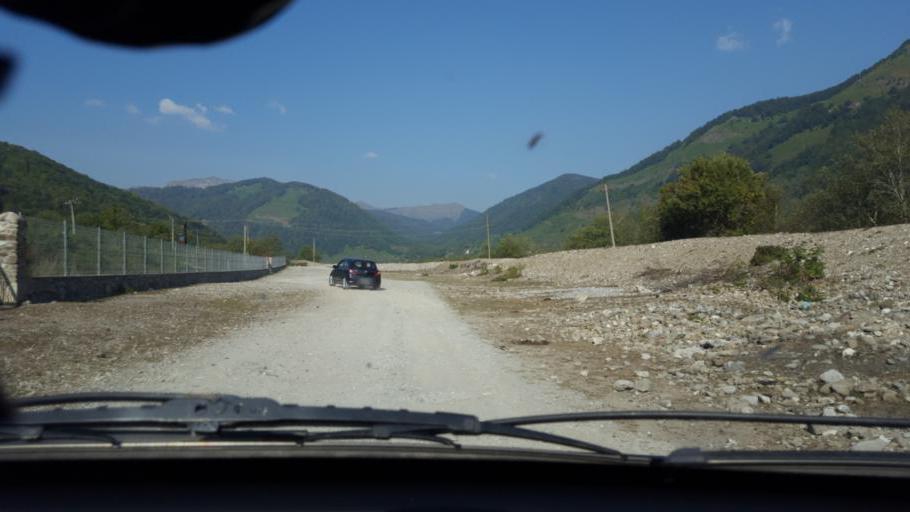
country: ME
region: Andrijevica
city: Andrijevica
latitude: 42.5934
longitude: 19.6822
